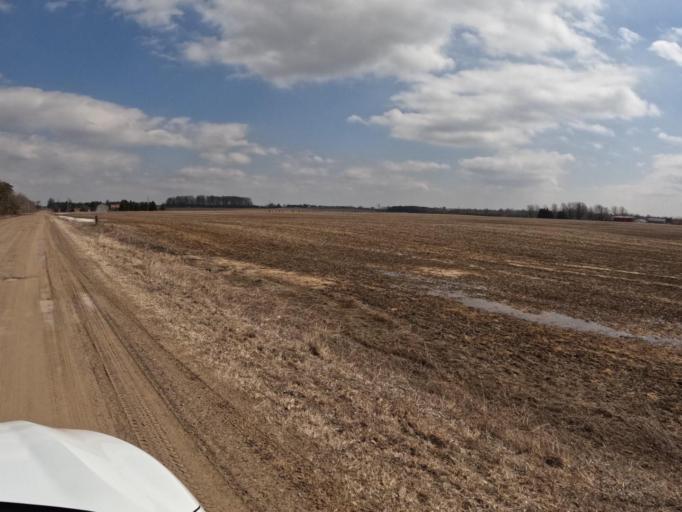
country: CA
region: Ontario
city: Shelburne
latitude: 44.0639
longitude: -80.2232
